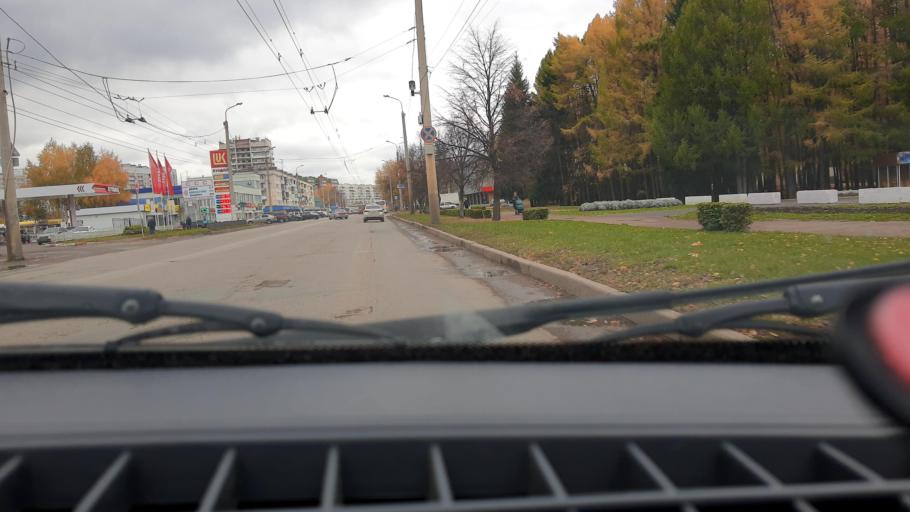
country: RU
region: Bashkortostan
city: Mikhaylovka
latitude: 54.7912
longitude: 55.8779
